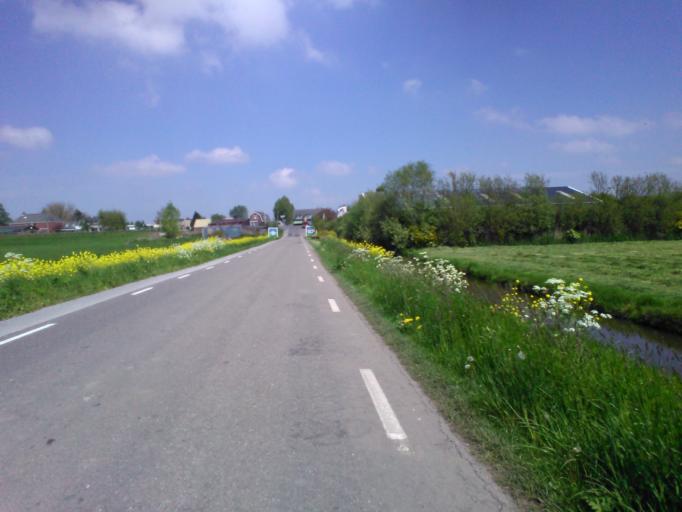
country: NL
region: South Holland
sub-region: Gemeente Boskoop
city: Boskoop
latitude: 52.0931
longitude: 4.6032
